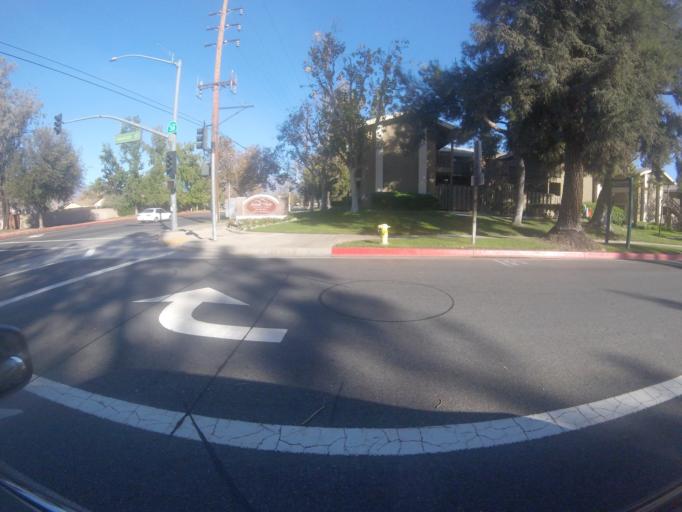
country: US
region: California
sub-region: San Bernardino County
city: Redlands
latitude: 34.0699
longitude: -117.1672
